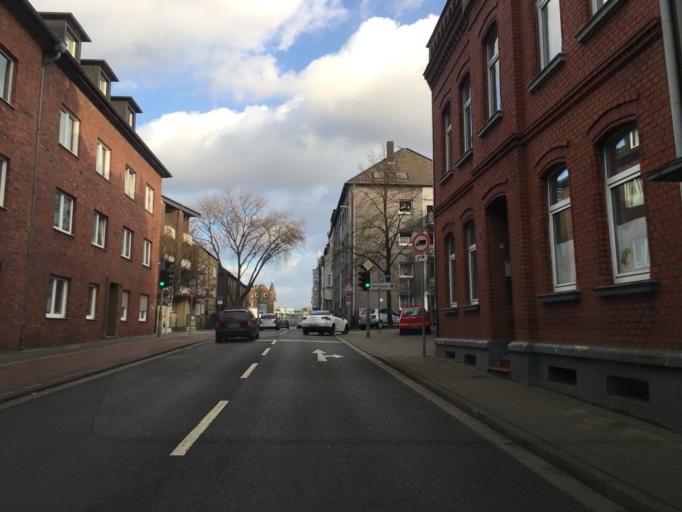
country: DE
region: North Rhine-Westphalia
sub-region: Regierungsbezirk Dusseldorf
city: Oberhausen
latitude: 51.5128
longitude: 6.8468
